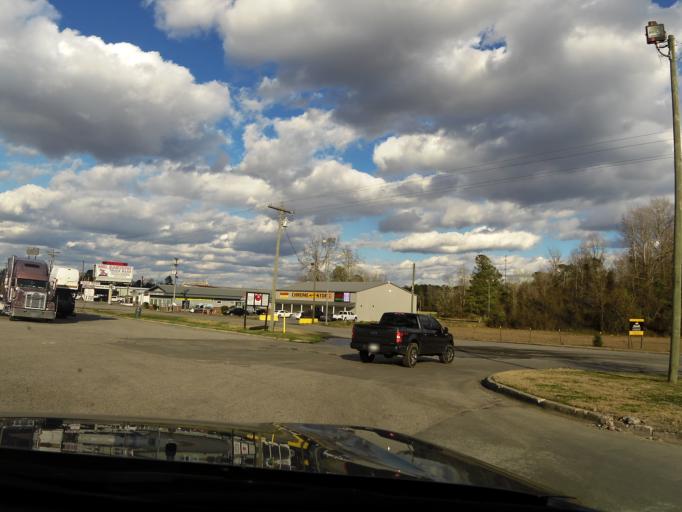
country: US
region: South Carolina
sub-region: Clarendon County
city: Manning
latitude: 33.7046
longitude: -80.2412
